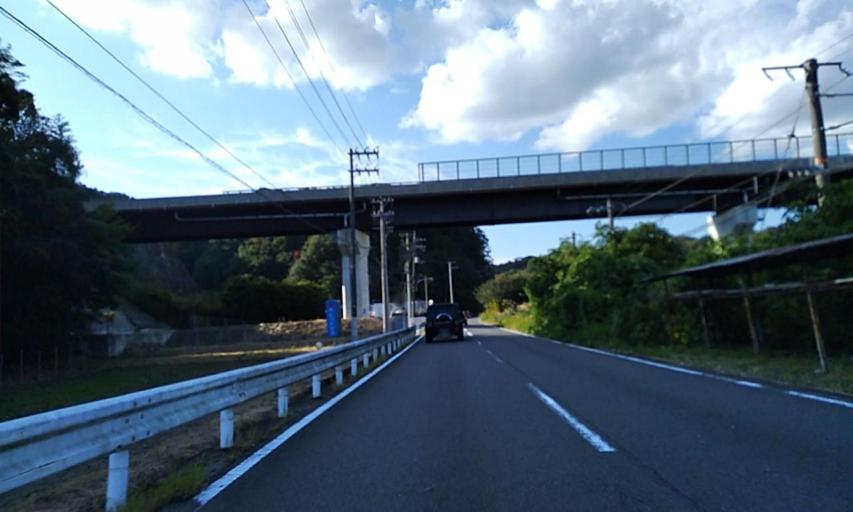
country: JP
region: Wakayama
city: Tanabe
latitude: 33.6814
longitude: 135.4060
